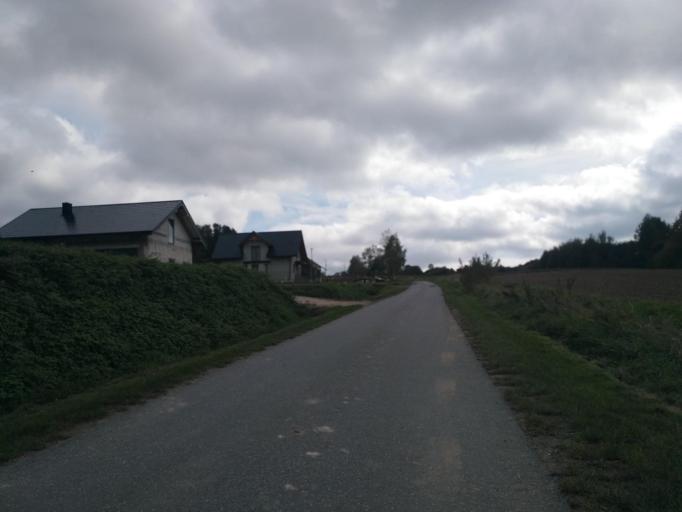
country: PL
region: Subcarpathian Voivodeship
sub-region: Powiat ropczycko-sedziszowski
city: Niedzwiada
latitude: 49.9285
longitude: 21.4812
